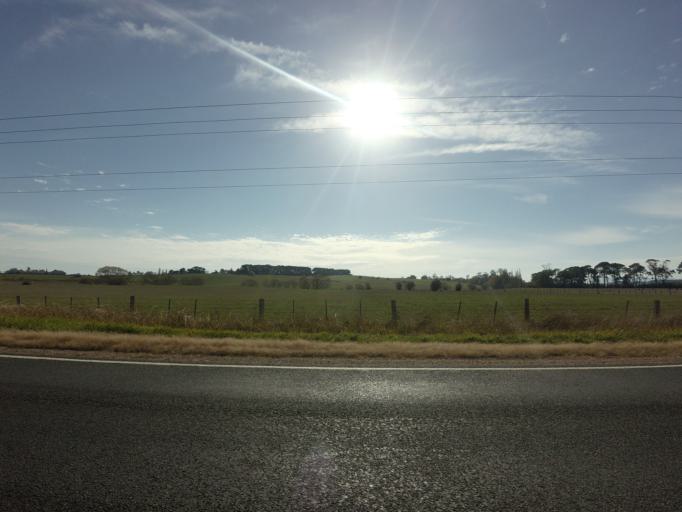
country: AU
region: Tasmania
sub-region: Meander Valley
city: Westbury
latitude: -41.5285
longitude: 146.9286
